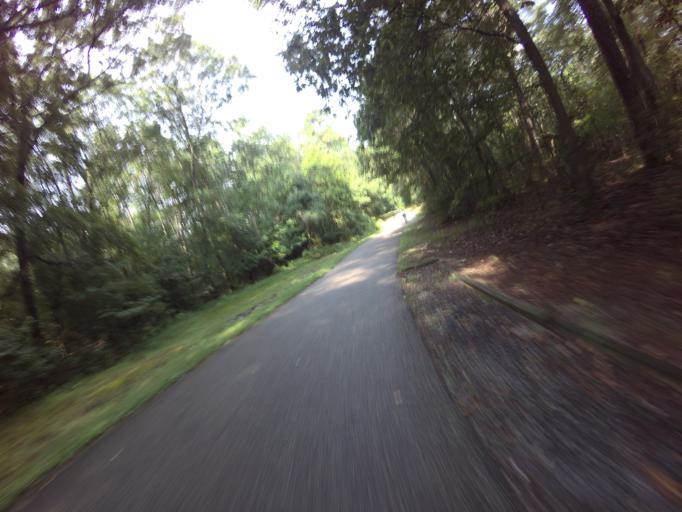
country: US
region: Maryland
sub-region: Anne Arundel County
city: Glen Burnie
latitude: 39.1585
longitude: -76.6504
